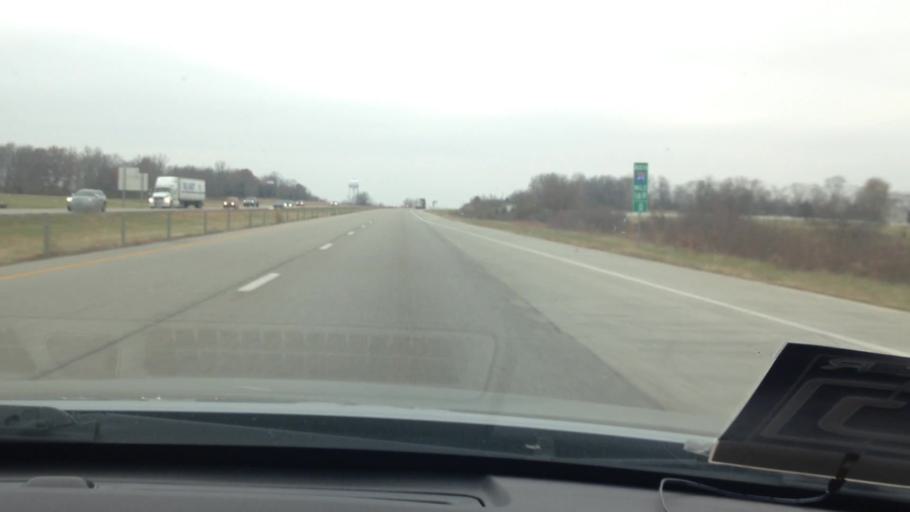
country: US
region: Missouri
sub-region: Cass County
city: Peculiar
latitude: 38.7432
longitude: -94.4737
